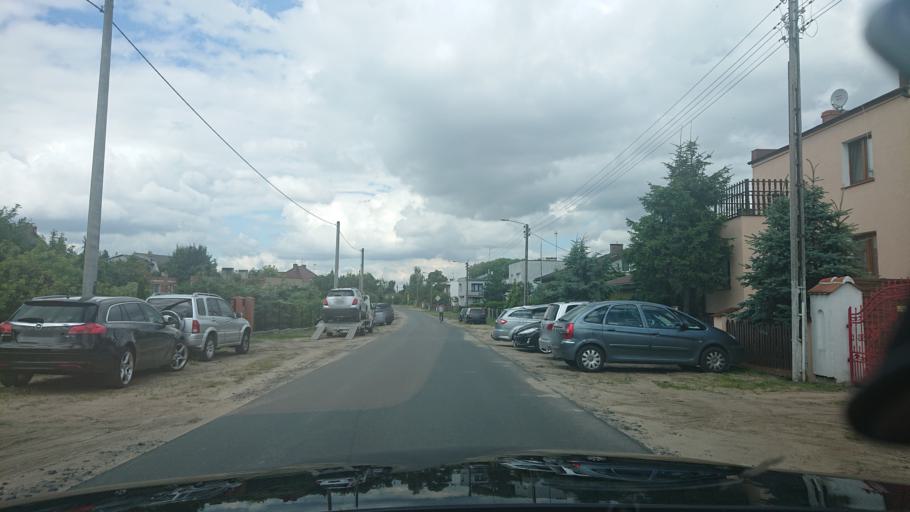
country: PL
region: Greater Poland Voivodeship
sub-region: Powiat gnieznienski
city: Gniezno
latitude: 52.5136
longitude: 17.6204
